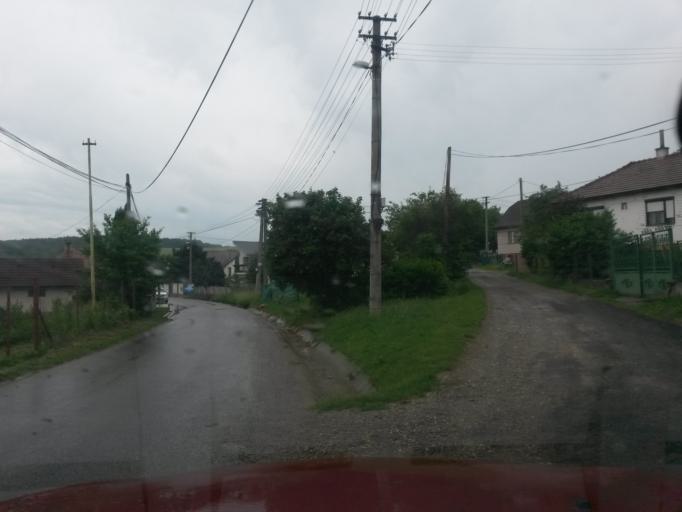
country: SK
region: Kosicky
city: Kosice
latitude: 48.7068
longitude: 21.1788
